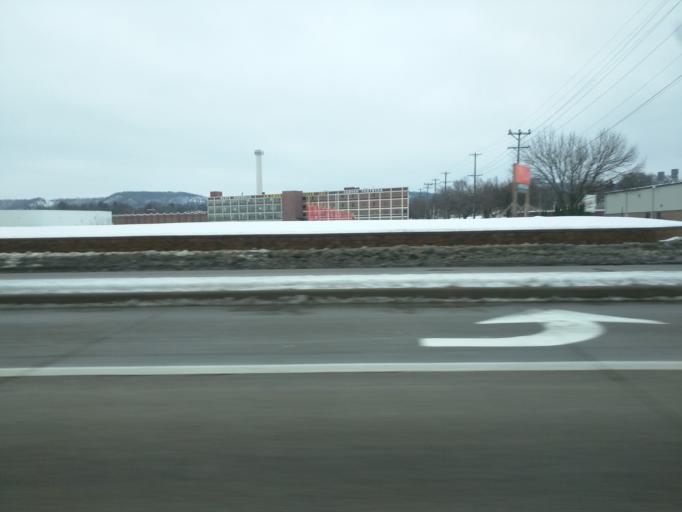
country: US
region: Wisconsin
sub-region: La Crosse County
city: North La Crosse
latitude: 43.8339
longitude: -91.2396
